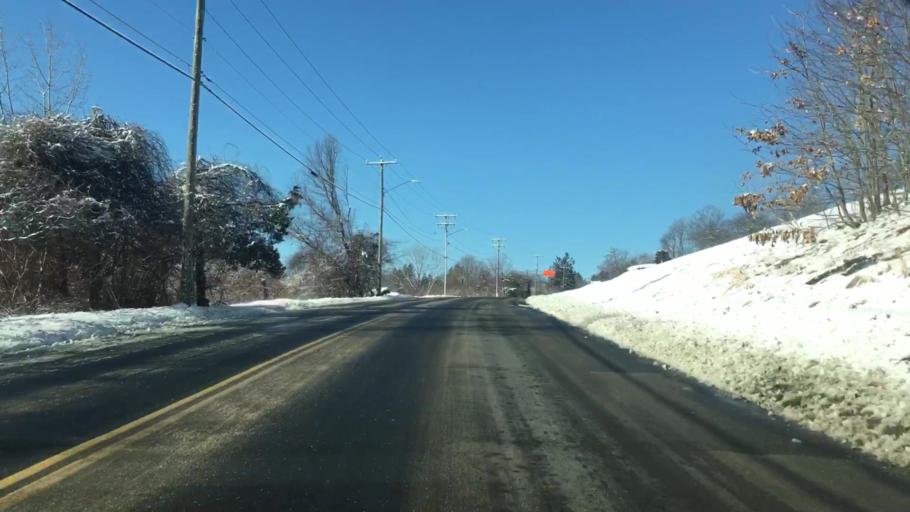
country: US
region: Connecticut
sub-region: Litchfield County
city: Oakville
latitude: 41.6094
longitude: -73.0788
